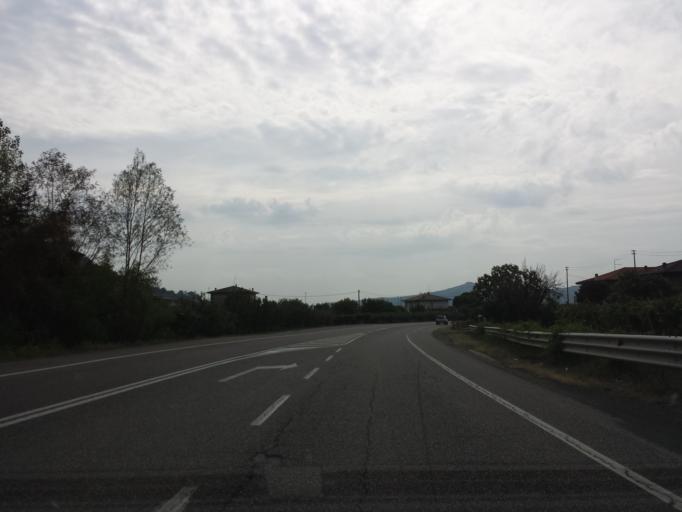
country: IT
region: Veneto
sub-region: Provincia di Verona
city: Montecchia di Crosara
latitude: 45.4949
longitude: 11.2533
